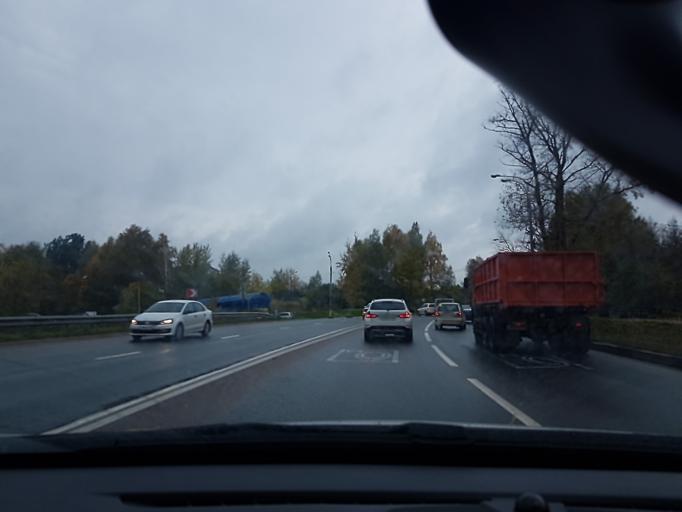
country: RU
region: Moskovskaya
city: Istra
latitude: 55.9161
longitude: 36.8418
